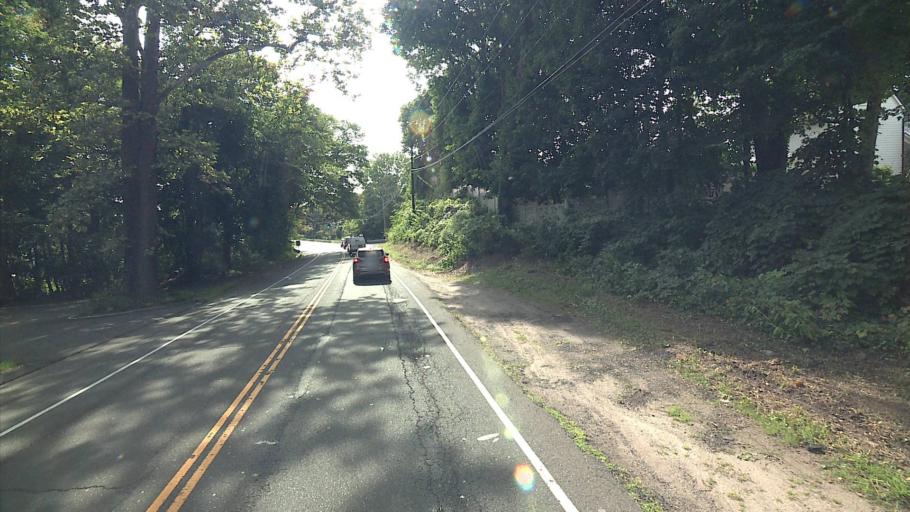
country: US
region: Connecticut
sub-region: Fairfield County
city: New Canaan
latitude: 41.1519
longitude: -73.4906
